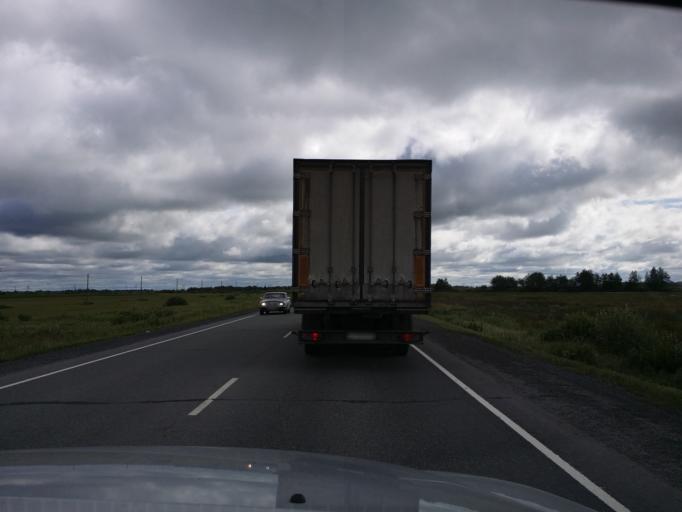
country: RU
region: Tjumen
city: Antipino
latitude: 57.1906
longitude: 65.9836
